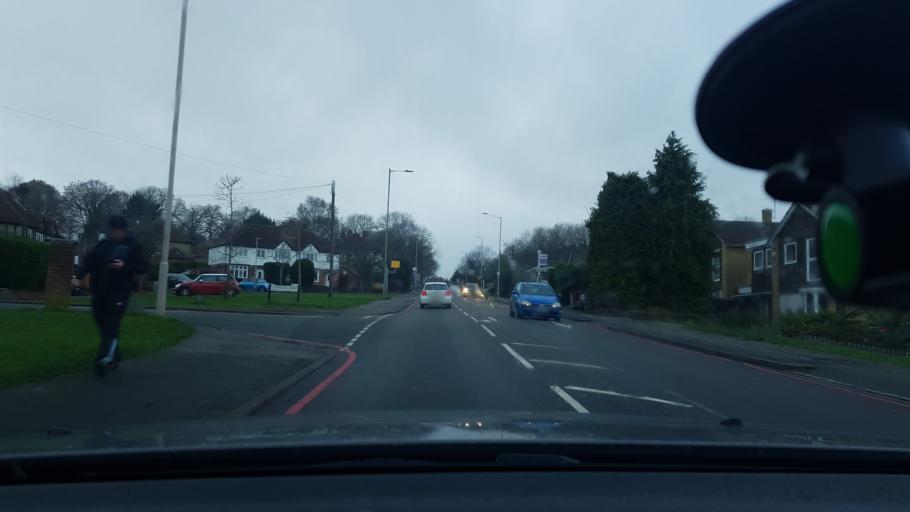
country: GB
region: England
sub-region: West Berkshire
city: Tilehurst
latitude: 51.4598
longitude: -1.0206
